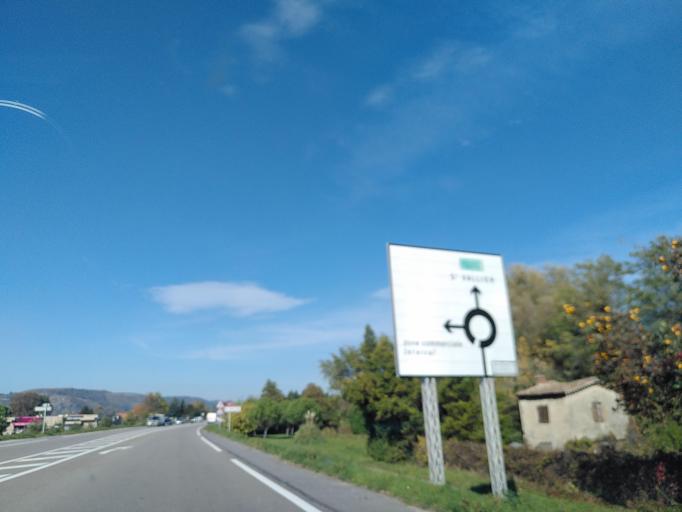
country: FR
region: Rhone-Alpes
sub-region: Departement de la Drome
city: Saint-Vallier
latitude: 45.1708
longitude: 4.8148
